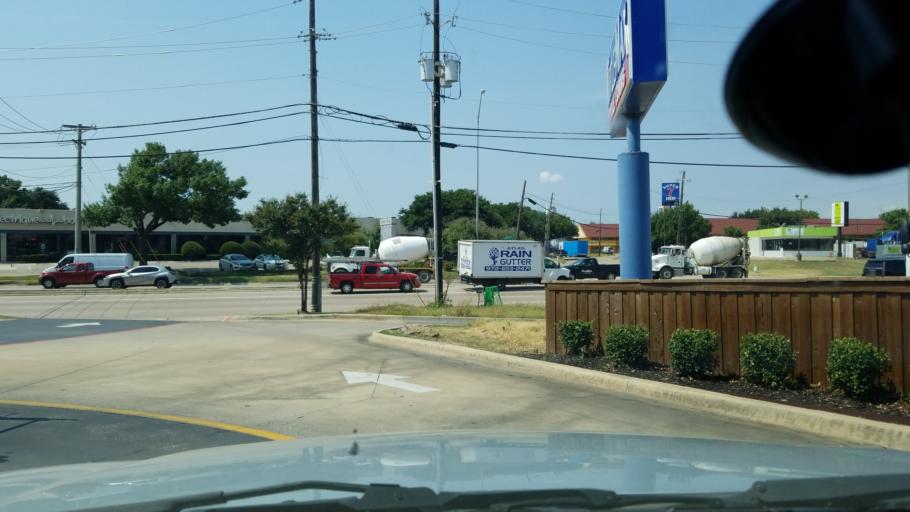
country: US
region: Texas
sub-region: Dallas County
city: Farmers Branch
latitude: 32.8655
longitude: -96.9016
